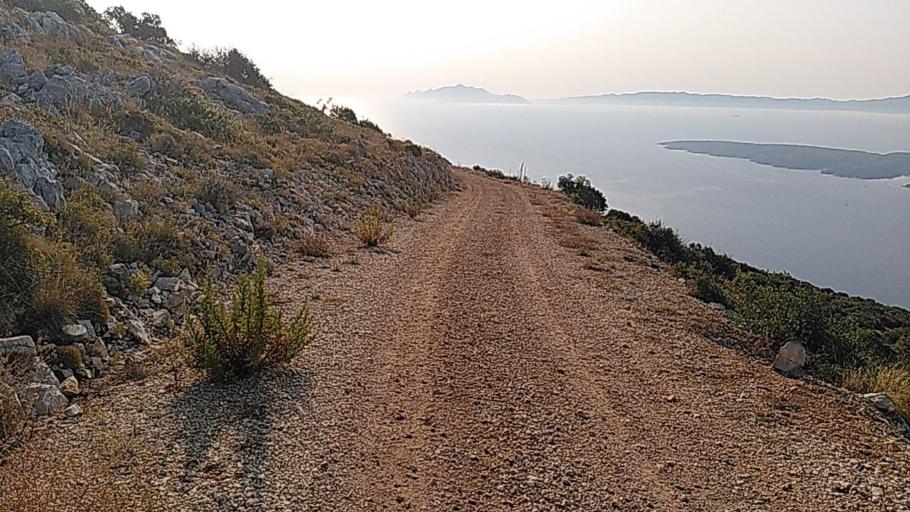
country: HR
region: Splitsko-Dalmatinska
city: Jelsa
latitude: 43.1337
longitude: 16.6616
